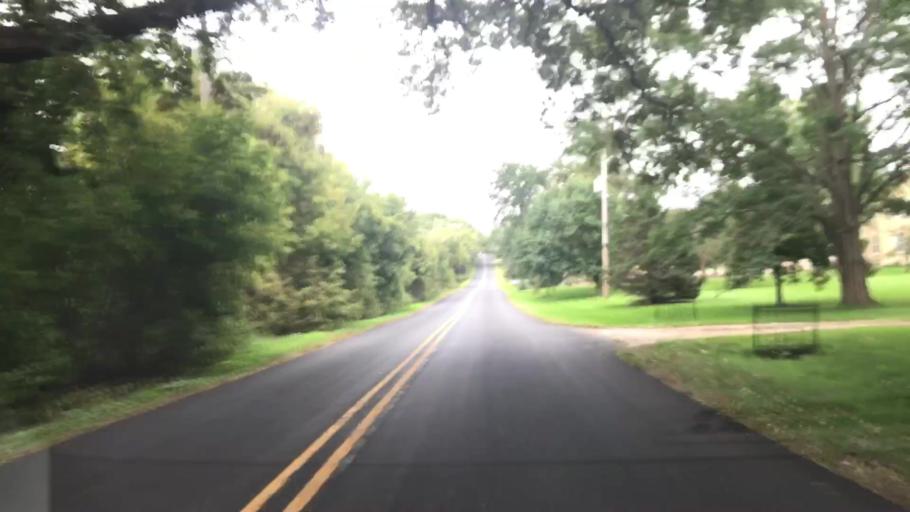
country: US
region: Wisconsin
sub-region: Waukesha County
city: North Prairie
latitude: 42.9151
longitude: -88.4201
